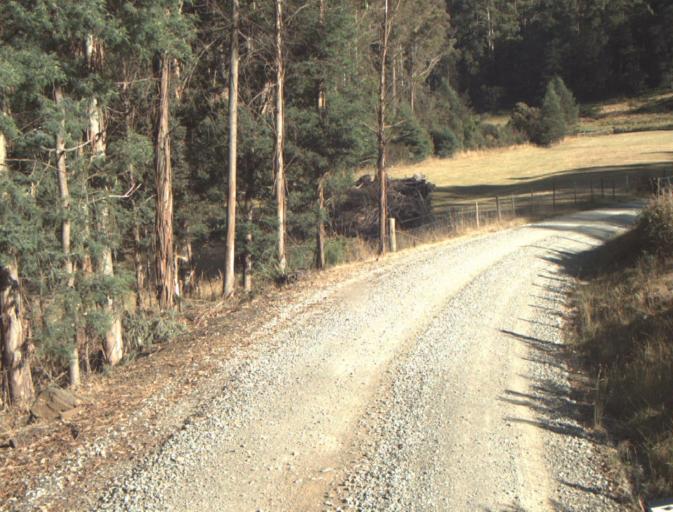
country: AU
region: Tasmania
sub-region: Launceston
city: Mayfield
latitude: -41.2893
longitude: 147.1972
